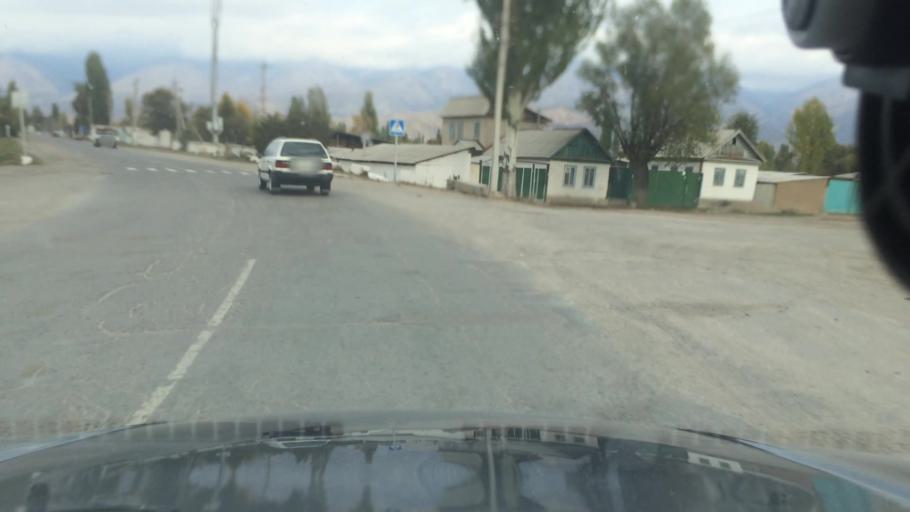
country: KG
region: Ysyk-Koel
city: Tyup
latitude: 42.7216
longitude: 78.3681
